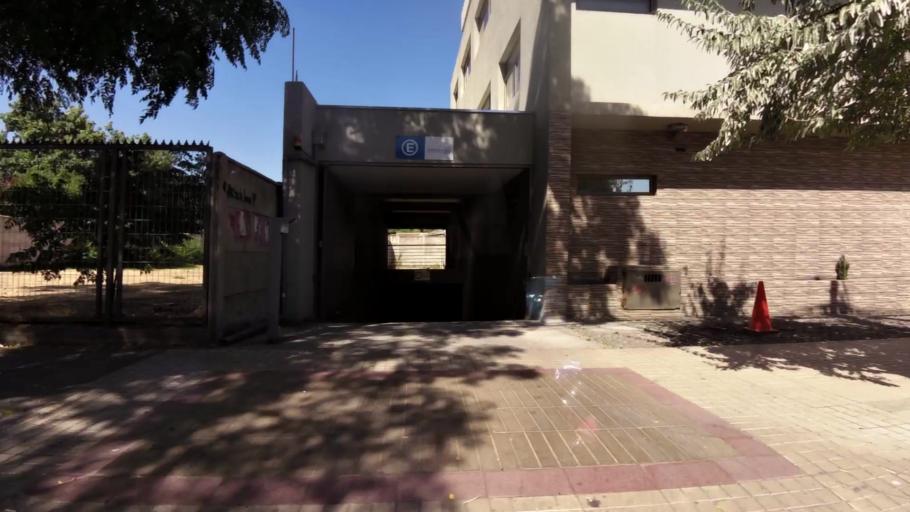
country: CL
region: Maule
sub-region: Provincia de Talca
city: Talca
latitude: -35.4238
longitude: -71.6595
